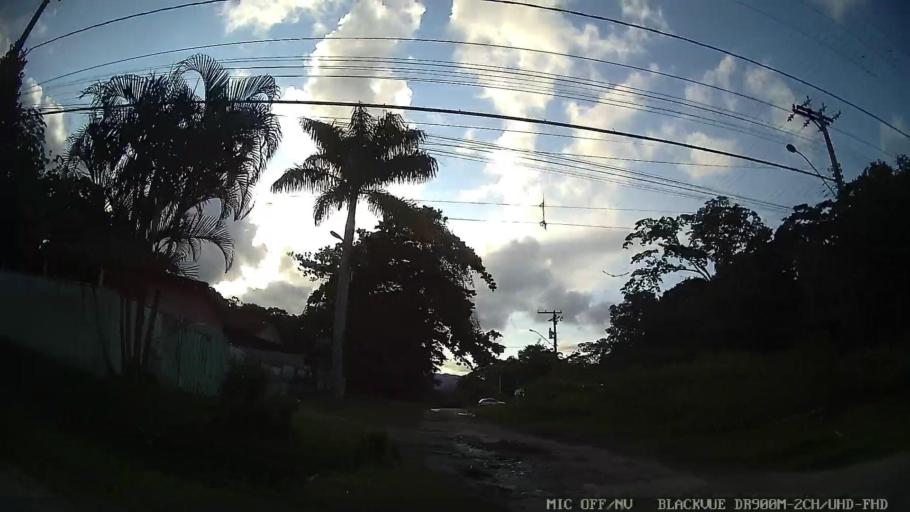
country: BR
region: Sao Paulo
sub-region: Itanhaem
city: Itanhaem
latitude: -24.1565
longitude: -46.8272
